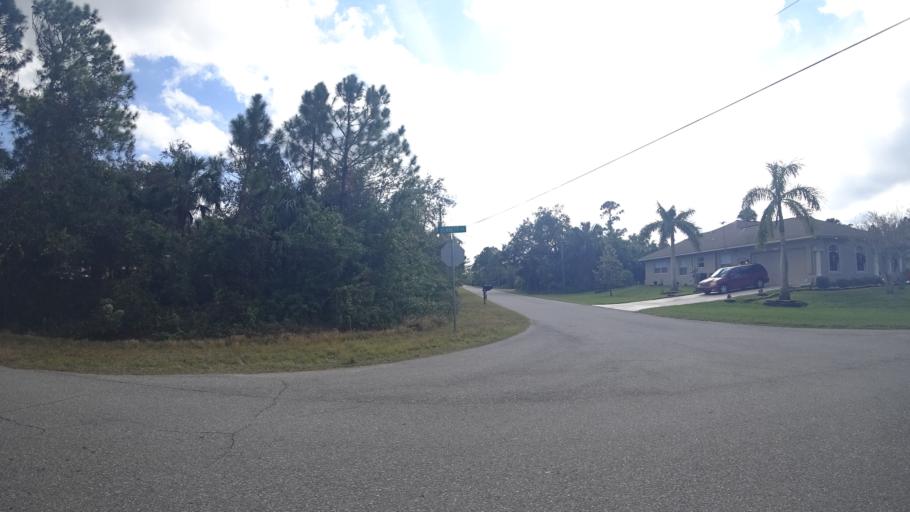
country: US
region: Florida
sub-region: Charlotte County
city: Port Charlotte
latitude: 27.0459
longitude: -82.1343
